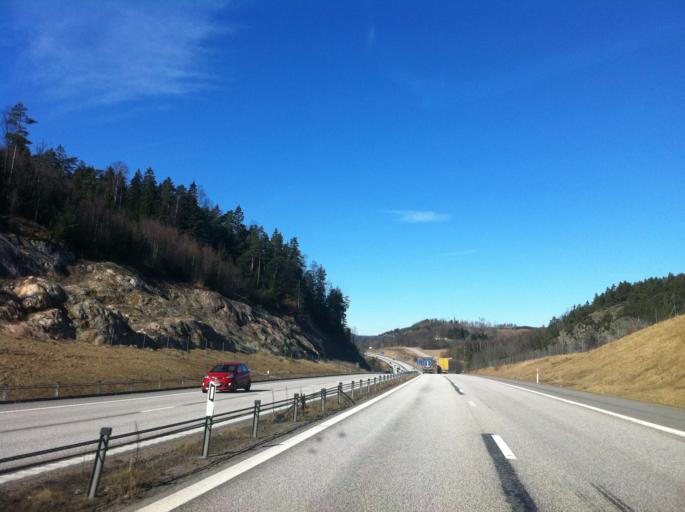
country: SE
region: Vaestra Goetaland
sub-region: Munkedals Kommun
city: Munkedal
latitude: 58.3789
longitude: 11.7756
